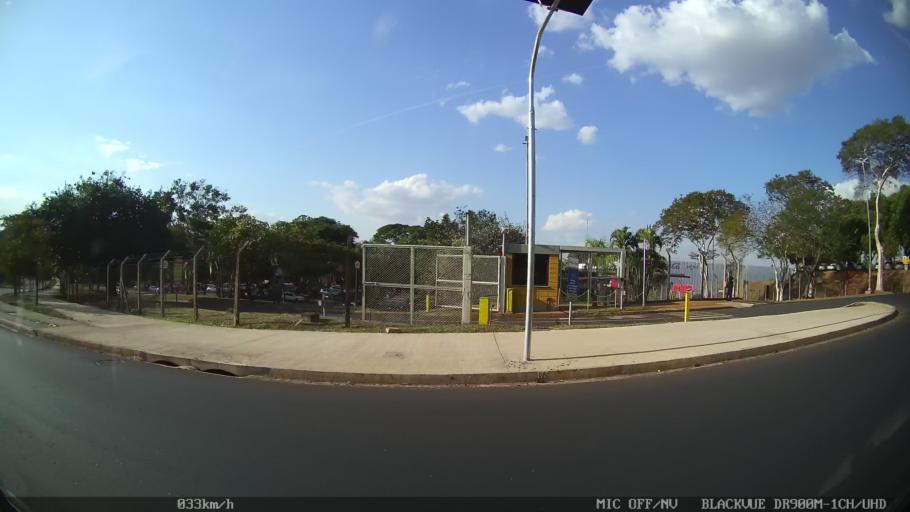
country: BR
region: Sao Paulo
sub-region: Ribeirao Preto
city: Ribeirao Preto
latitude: -21.1468
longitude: -47.8309
